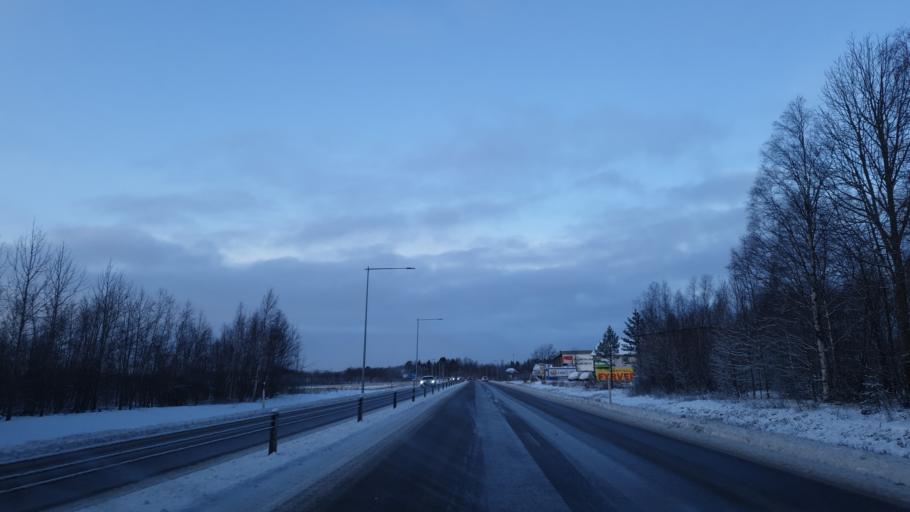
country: SE
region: Vaesterbotten
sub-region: Umea Kommun
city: Umea
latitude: 63.8010
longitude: 20.2714
